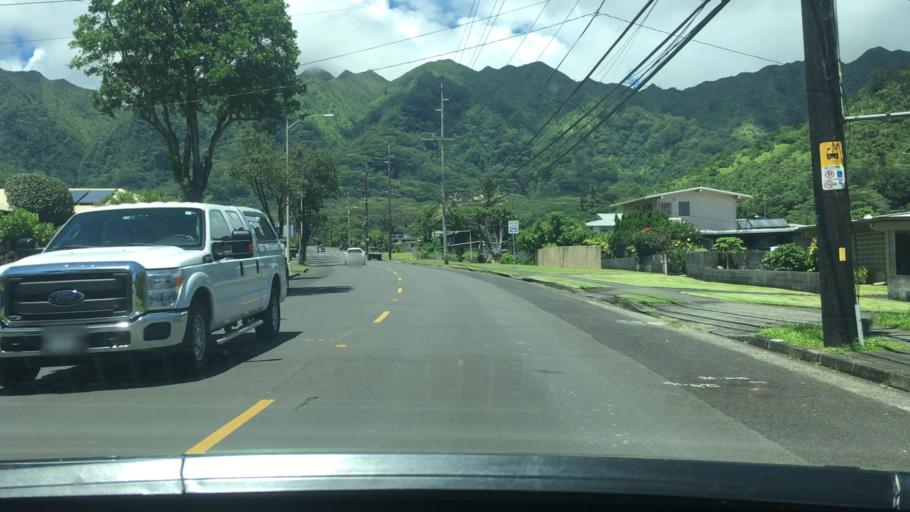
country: US
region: Hawaii
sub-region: Honolulu County
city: Honolulu
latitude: 21.3219
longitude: -157.8045
